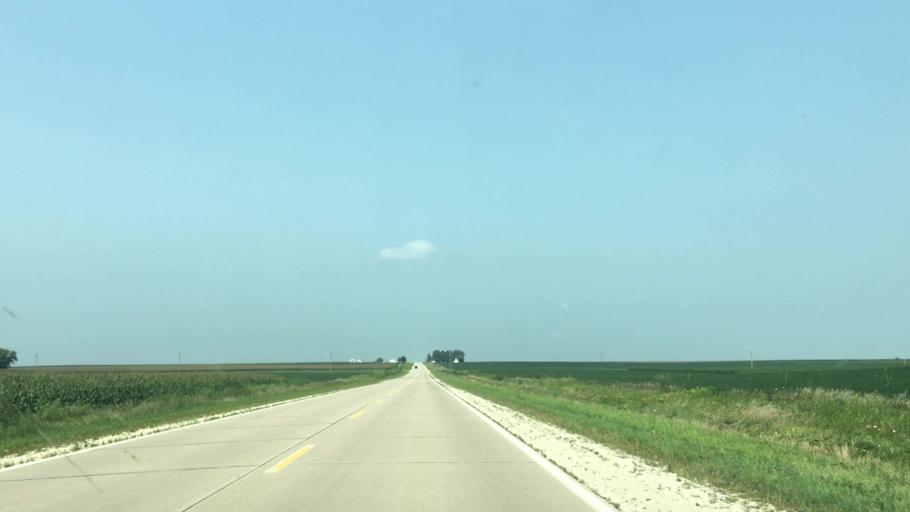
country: US
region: Iowa
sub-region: Fayette County
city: Oelwein
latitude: 42.6981
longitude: -91.8049
